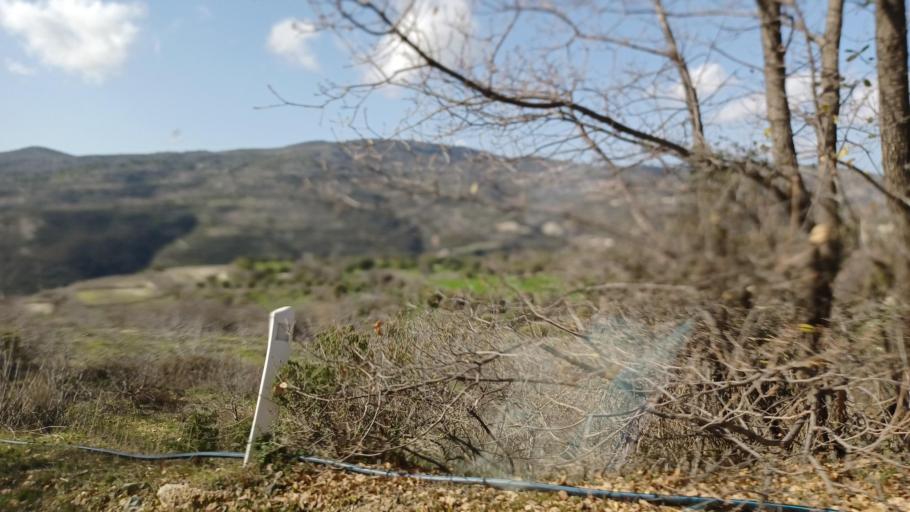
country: CY
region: Limassol
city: Pachna
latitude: 34.8449
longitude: 32.7313
